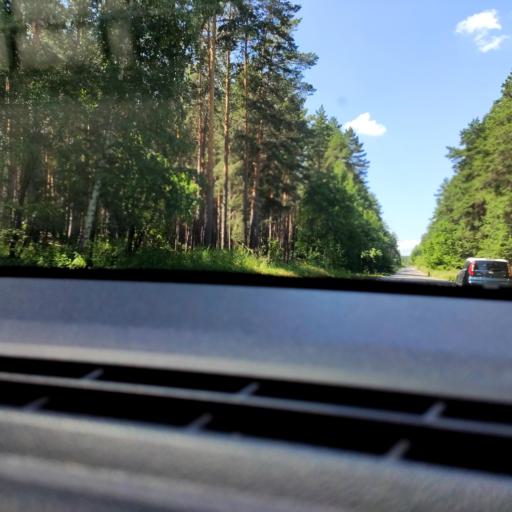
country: RU
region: Samara
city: Podstepki
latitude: 53.5734
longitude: 49.0436
